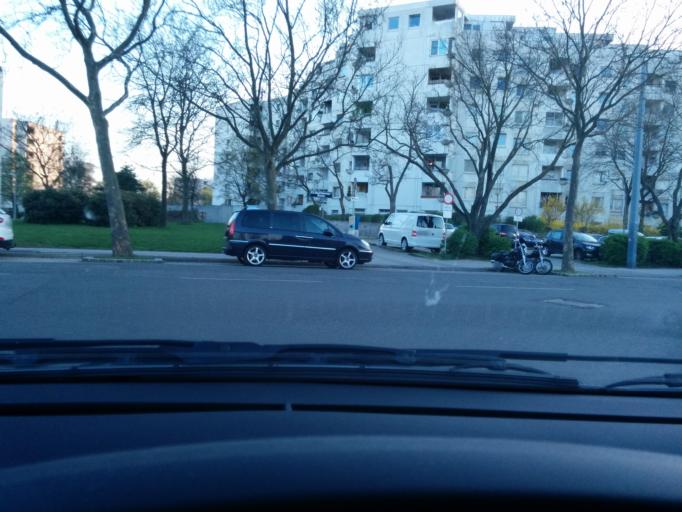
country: AT
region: Lower Austria
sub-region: Politischer Bezirk Modling
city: Vosendorf
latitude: 48.1323
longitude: 16.3149
